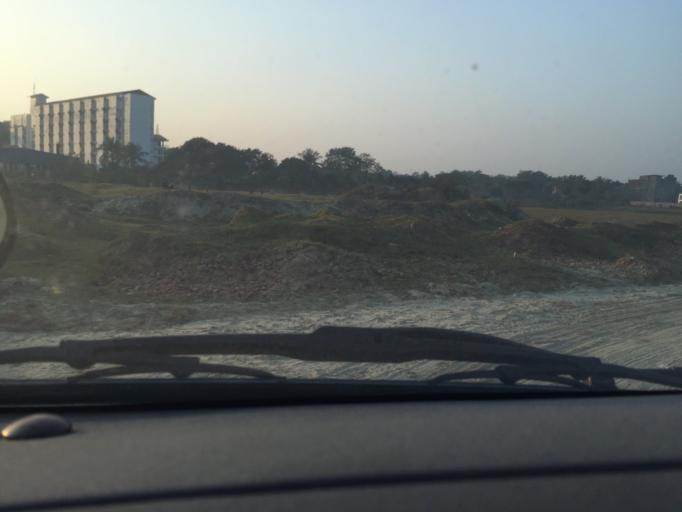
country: BD
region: Dhaka
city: Tungi
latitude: 23.8671
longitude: 90.3134
